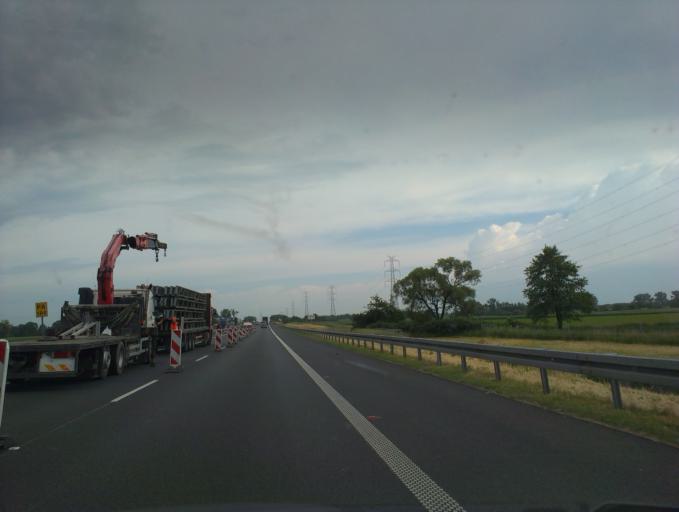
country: PL
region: Lower Silesian Voivodeship
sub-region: Powiat strzelinski
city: Wiazow
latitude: 50.8124
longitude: 17.3117
